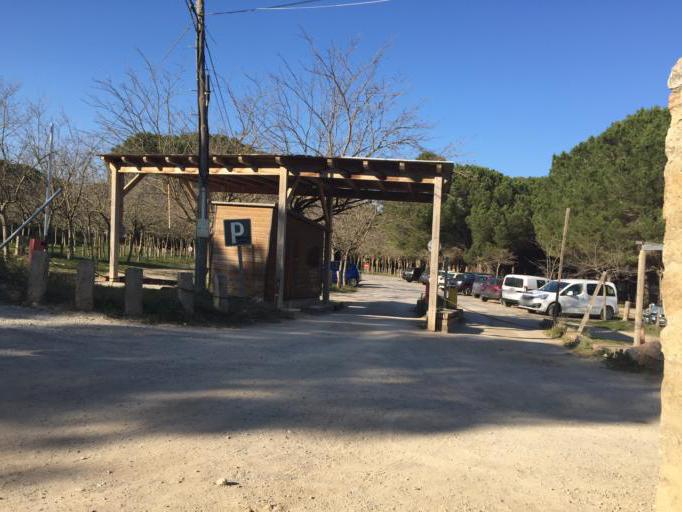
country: ES
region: Catalonia
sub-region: Provincia de Girona
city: l'Escala
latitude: 42.1316
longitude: 3.1211
